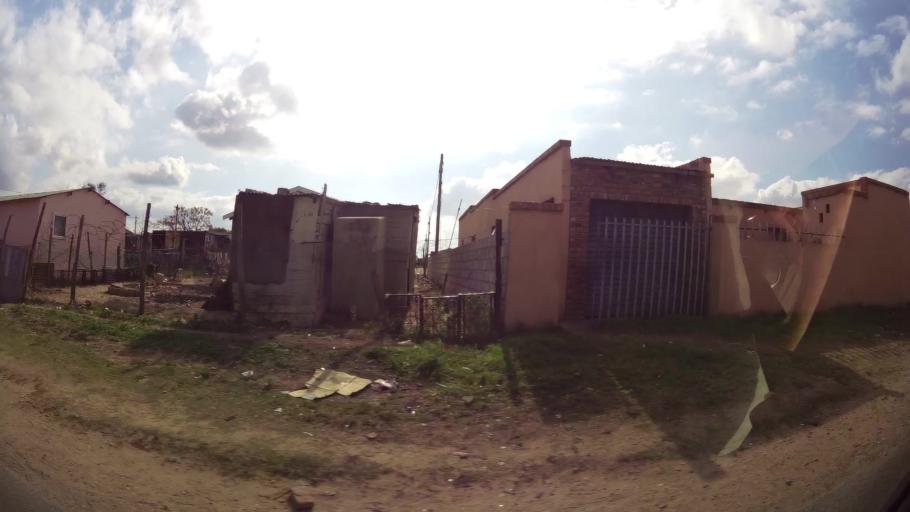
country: ZA
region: Eastern Cape
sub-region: Nelson Mandela Bay Metropolitan Municipality
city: Port Elizabeth
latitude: -33.7887
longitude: 25.5836
